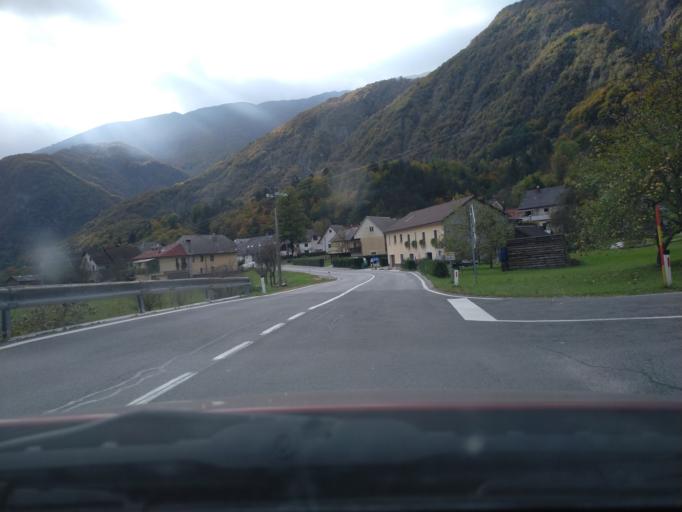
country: SI
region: Bovec
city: Bovec
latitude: 46.3059
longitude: 13.4813
